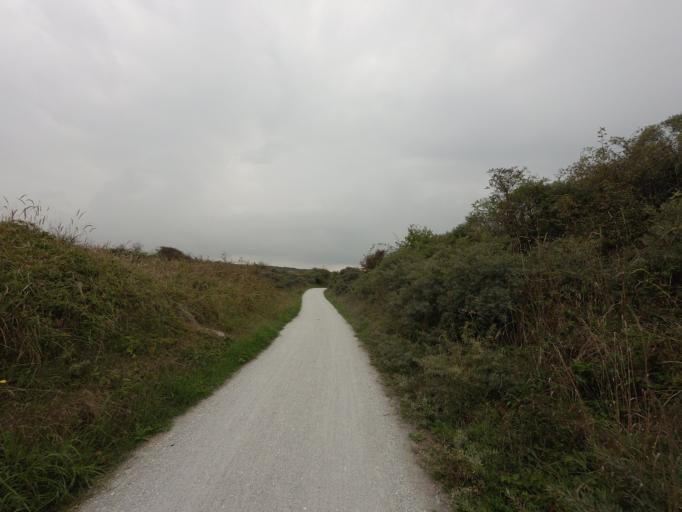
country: NL
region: Friesland
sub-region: Gemeente Schiermonnikoog
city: Schiermonnikoog
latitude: 53.4968
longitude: 6.1814
